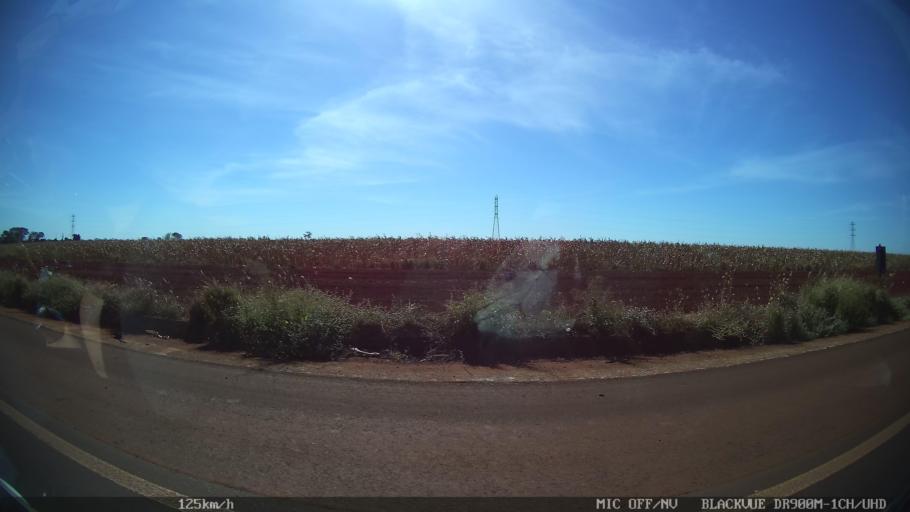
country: BR
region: Sao Paulo
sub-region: Guaira
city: Guaira
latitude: -20.4445
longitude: -48.3714
